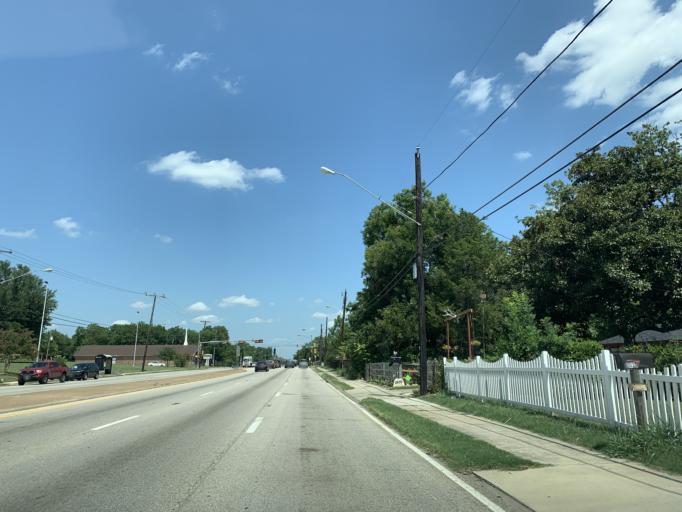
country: US
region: Texas
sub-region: Dallas County
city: Hutchins
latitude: 32.6898
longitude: -96.7816
